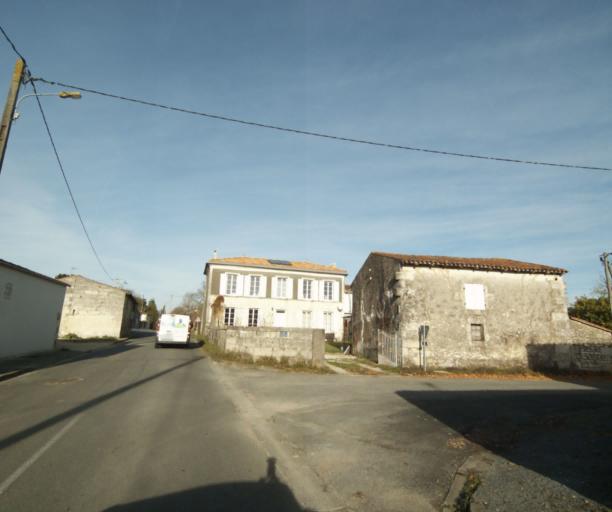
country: FR
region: Poitou-Charentes
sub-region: Departement de la Charente-Maritime
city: Chaniers
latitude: 45.7318
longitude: -0.5578
